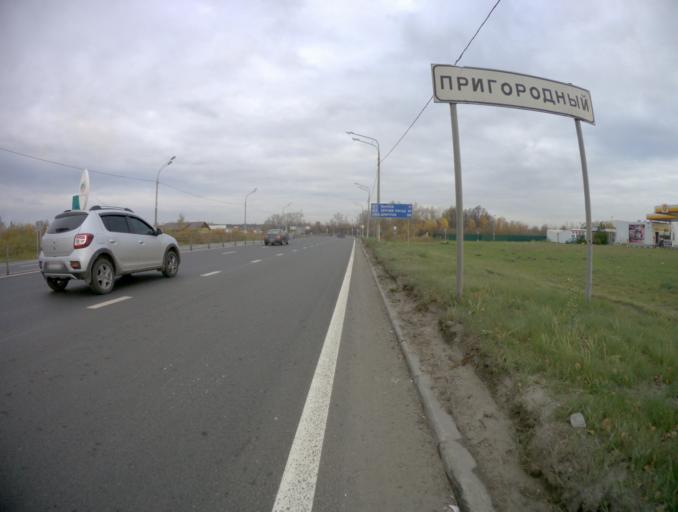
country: RU
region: Moskovskaya
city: Orekhovo-Zuyevo
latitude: 55.8384
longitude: 38.9708
